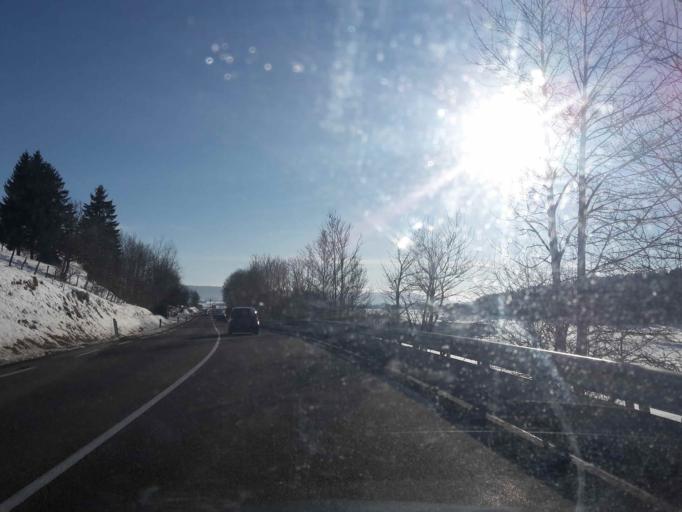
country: FR
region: Franche-Comte
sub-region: Departement du Doubs
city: Doubs
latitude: 46.9624
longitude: 6.3431
